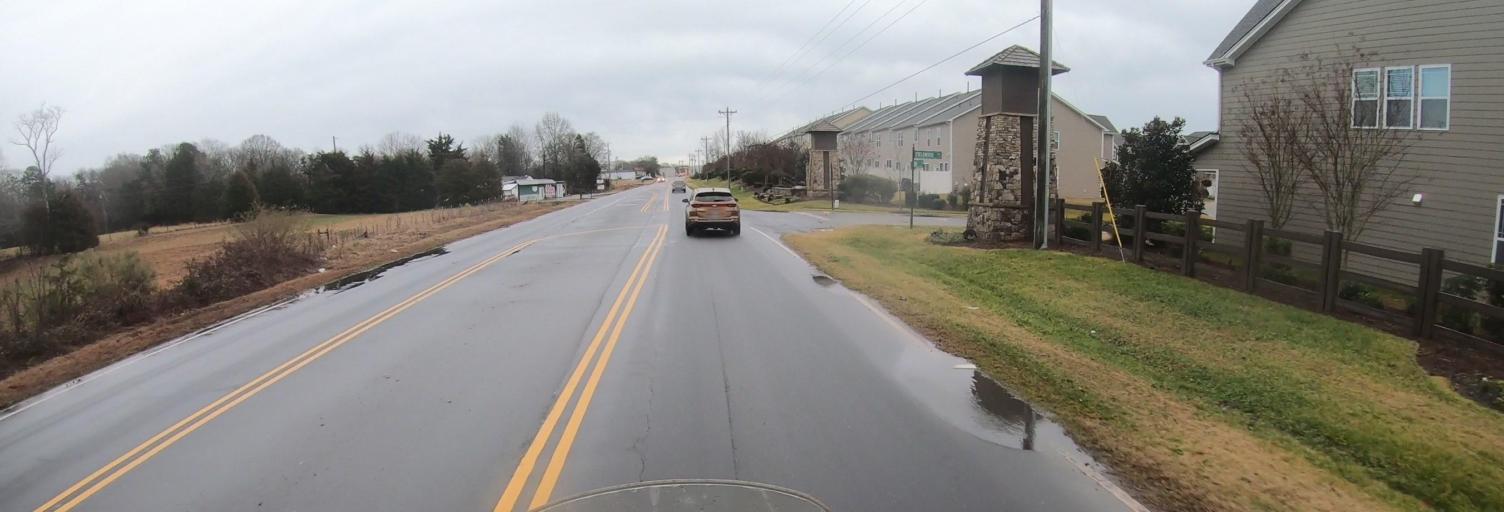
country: US
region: South Carolina
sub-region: York County
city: Tega Cay
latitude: 35.0688
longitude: -80.9951
